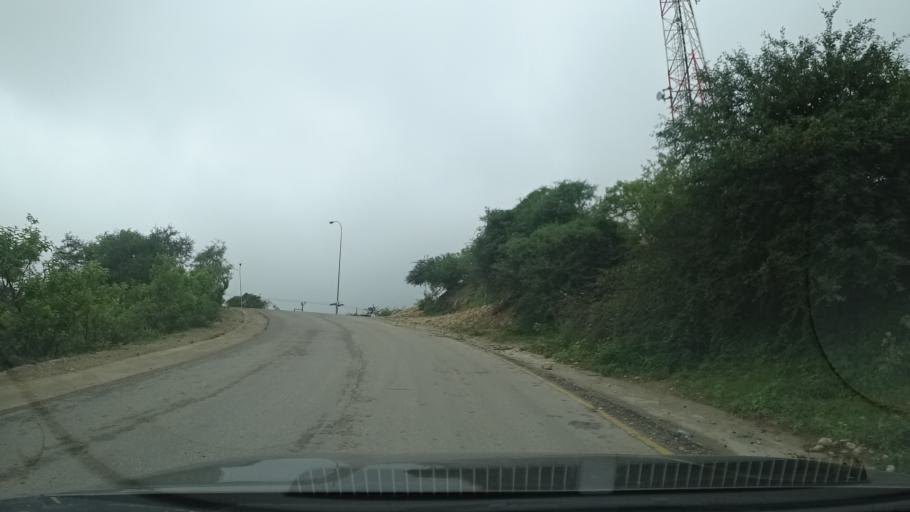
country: OM
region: Zufar
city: Salalah
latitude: 17.1010
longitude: 54.0731
